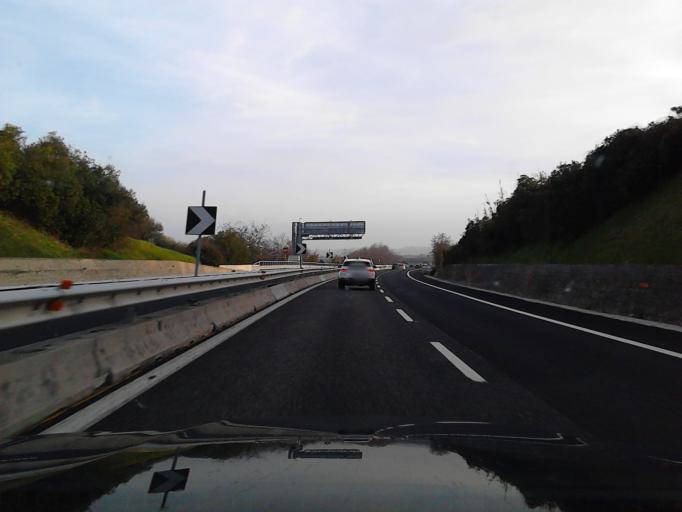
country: IT
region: Abruzzo
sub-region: Provincia di Chieti
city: Ortona
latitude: 42.3218
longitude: 14.3966
